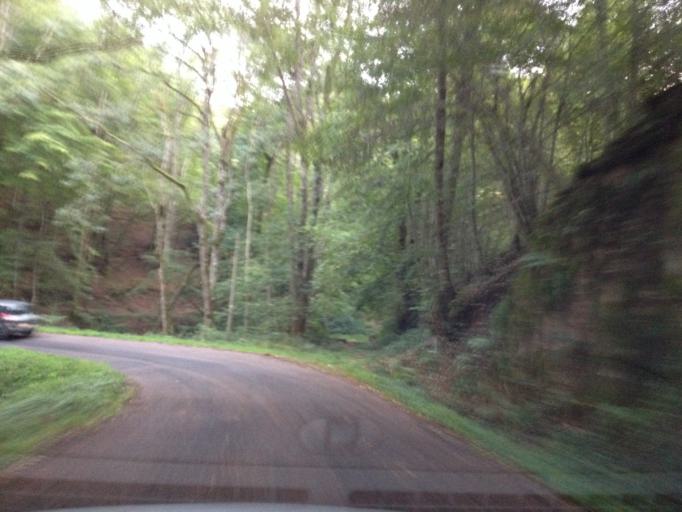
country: FR
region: Rhone-Alpes
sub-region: Departement de la Loire
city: Renaison
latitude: 46.0184
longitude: 3.8648
